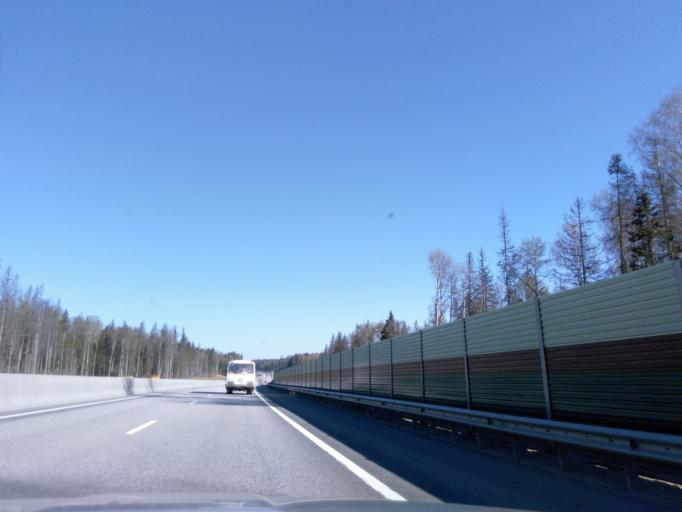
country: RU
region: Moskovskaya
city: Rzhavki
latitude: 56.0298
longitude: 37.2712
